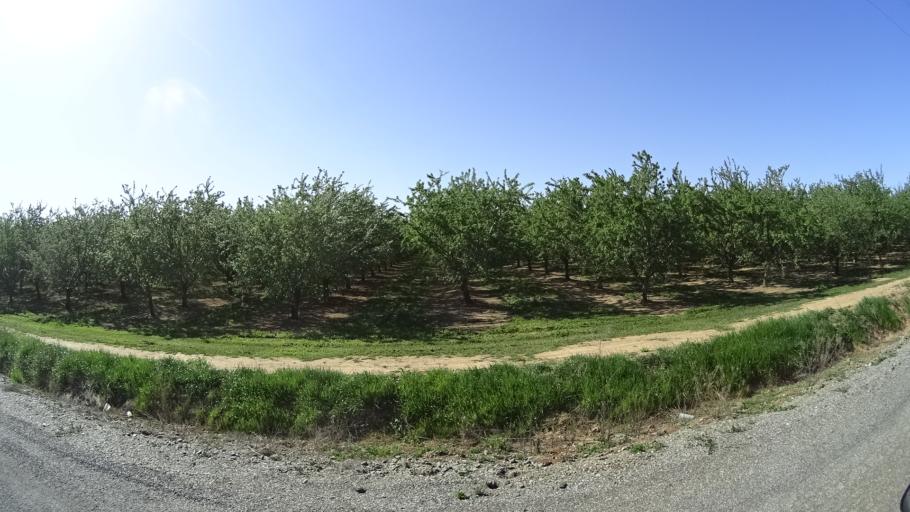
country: US
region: California
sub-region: Glenn County
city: Hamilton City
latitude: 39.7756
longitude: -122.0730
